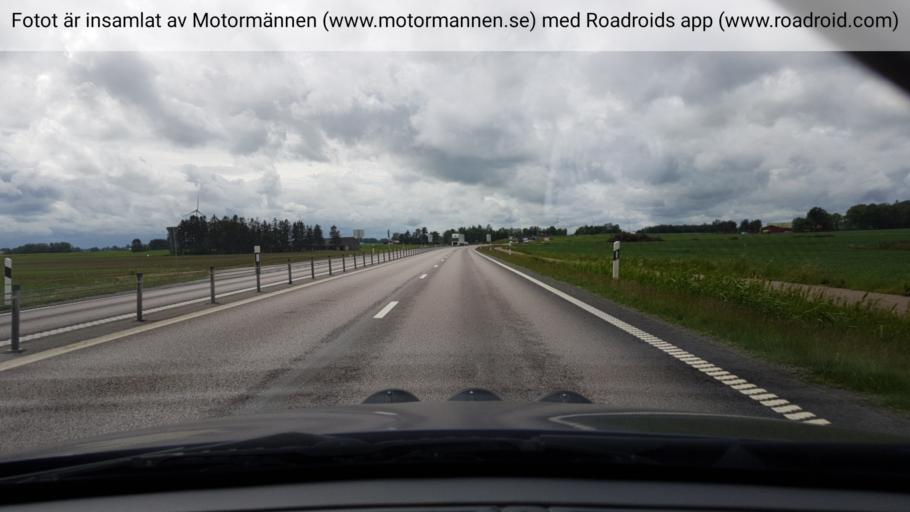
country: SE
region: Vaestra Goetaland
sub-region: Vara Kommun
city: Vara
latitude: 58.2944
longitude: 13.0542
